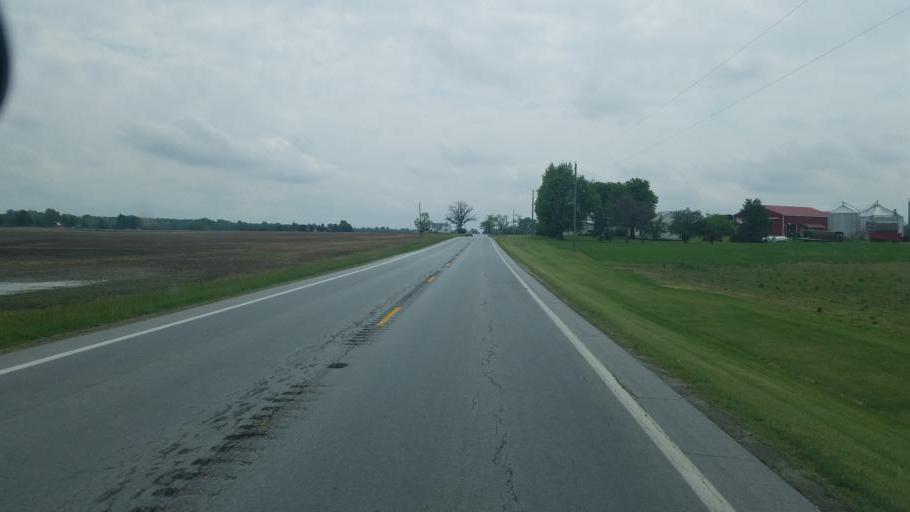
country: US
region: Ohio
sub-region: Union County
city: Richwood
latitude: 40.3643
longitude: -83.2924
